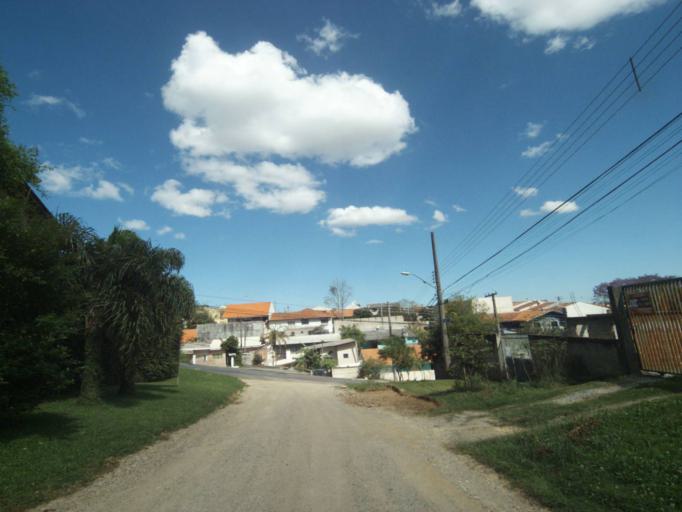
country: BR
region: Parana
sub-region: Curitiba
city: Curitiba
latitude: -25.3743
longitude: -49.2479
